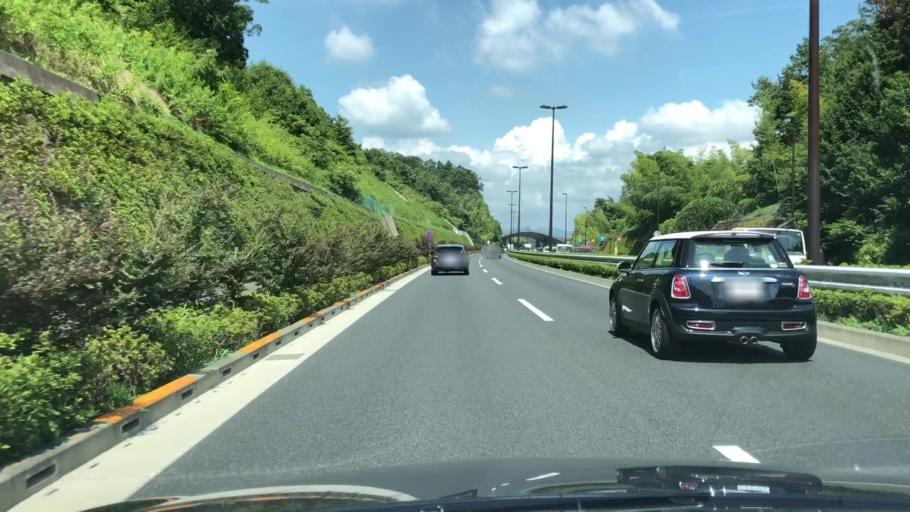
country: JP
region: Tokyo
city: Fussa
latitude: 35.6995
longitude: 139.3132
